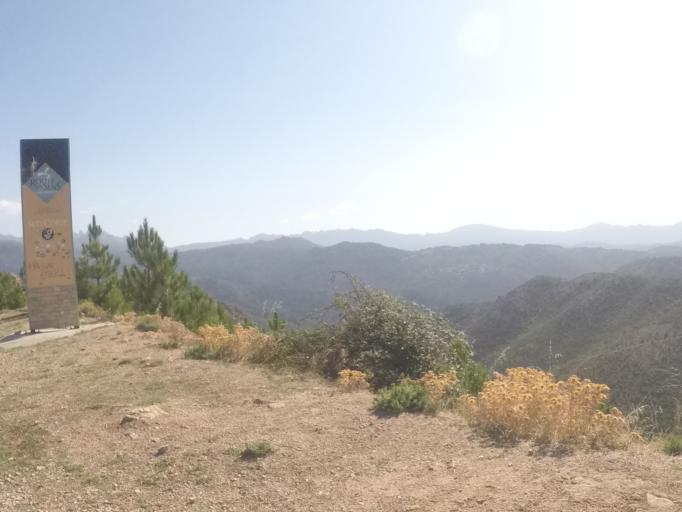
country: FR
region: Corsica
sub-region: Departement de la Corse-du-Sud
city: Olmeto
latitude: 41.7608
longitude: 9.0317
